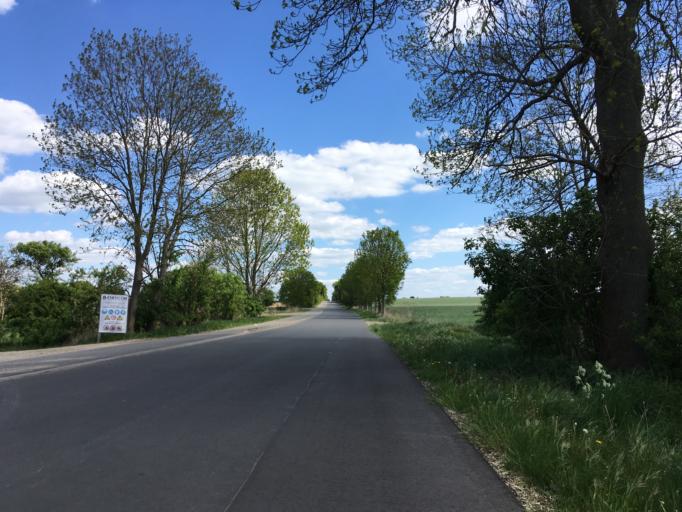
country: DE
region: Brandenburg
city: Wandlitz
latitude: 52.7877
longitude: 13.4630
